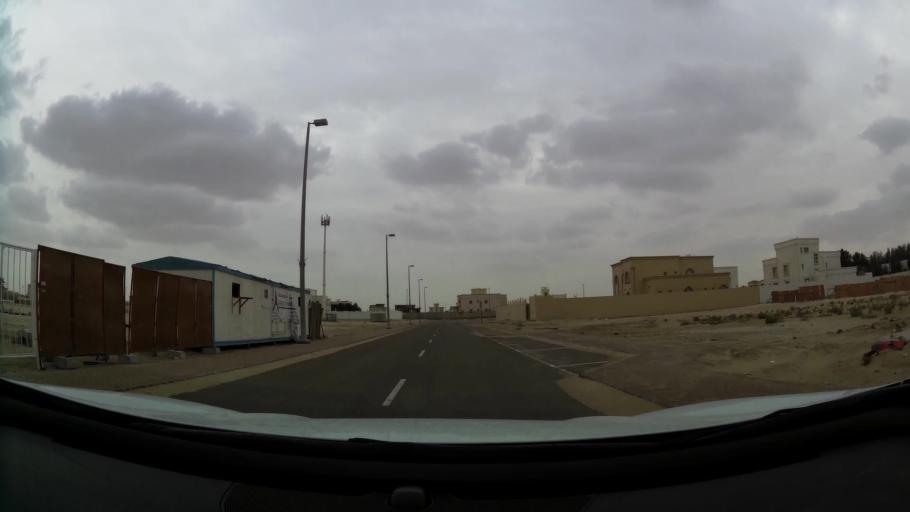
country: AE
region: Abu Dhabi
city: Abu Dhabi
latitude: 24.3713
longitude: 54.6289
